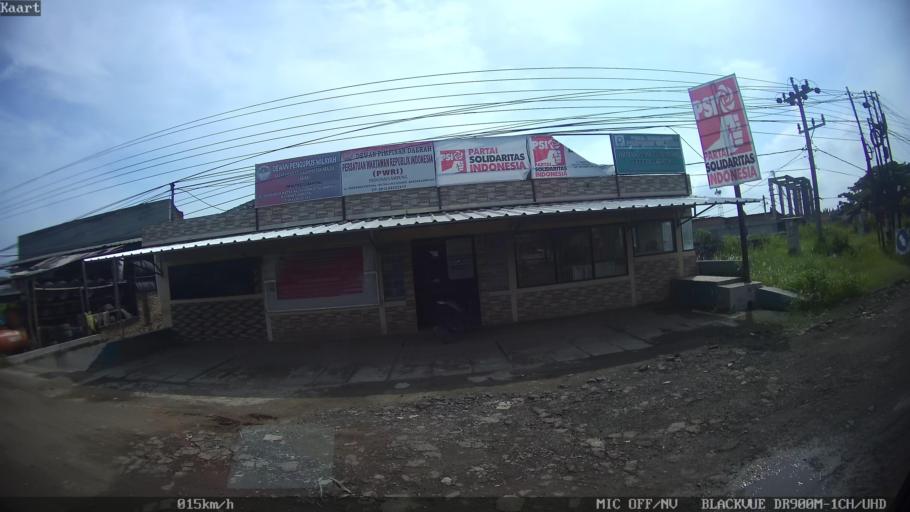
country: ID
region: Lampung
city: Kedaton
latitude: -5.3754
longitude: 105.2793
